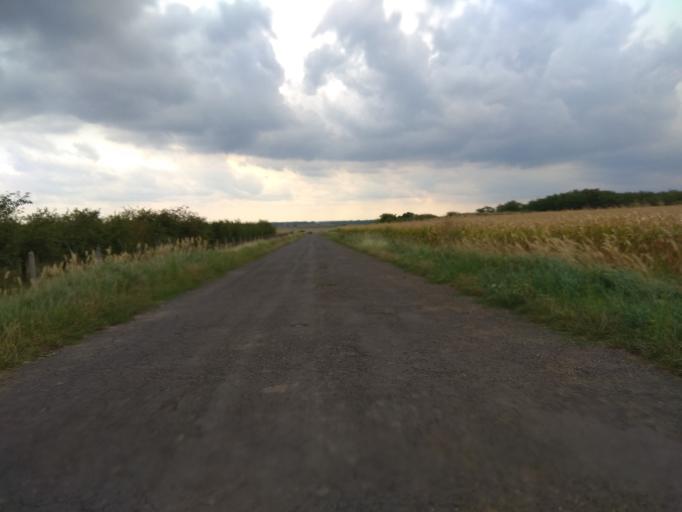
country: HU
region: Borsod-Abauj-Zemplen
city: Bekecs
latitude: 48.1522
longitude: 21.1154
